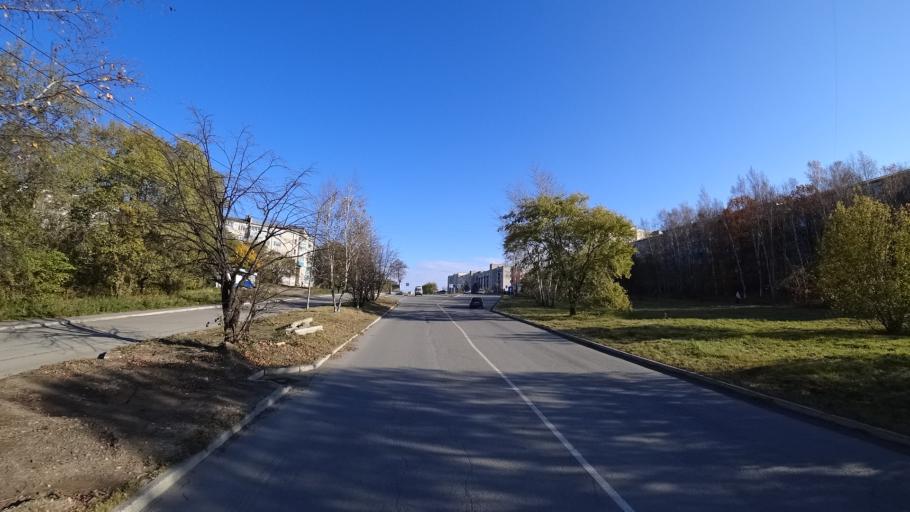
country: RU
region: Khabarovsk Krai
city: Amursk
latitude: 50.2409
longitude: 136.9128
